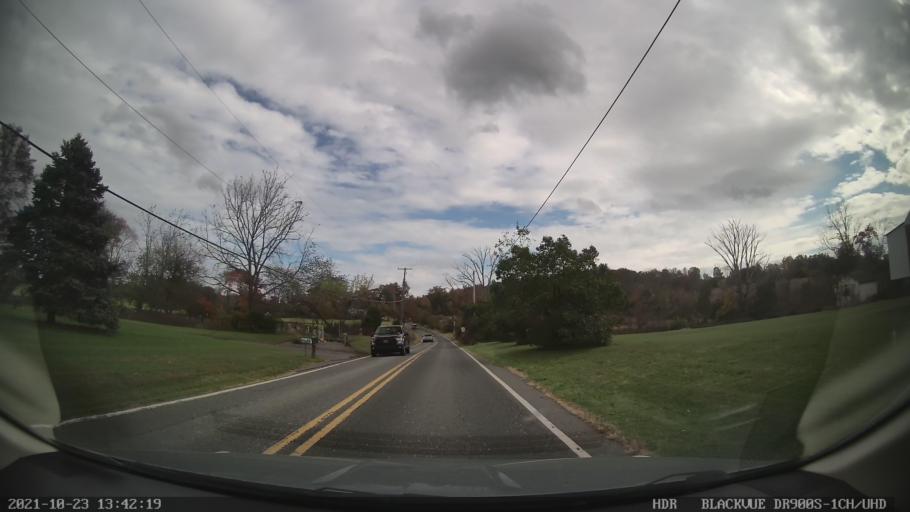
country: US
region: Pennsylvania
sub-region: Berks County
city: Bally
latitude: 40.4077
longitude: -75.5548
